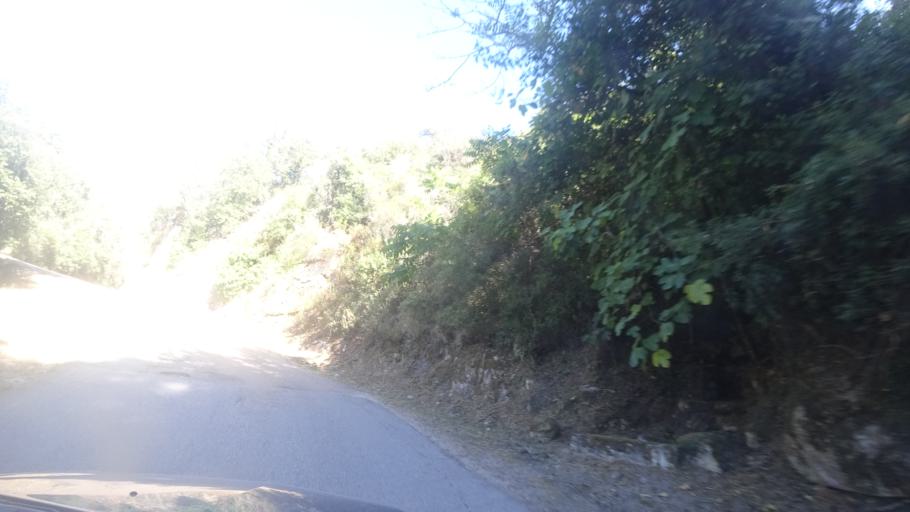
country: FR
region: Corsica
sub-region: Departement de la Corse-du-Sud
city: Cargese
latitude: 42.2633
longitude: 8.6952
